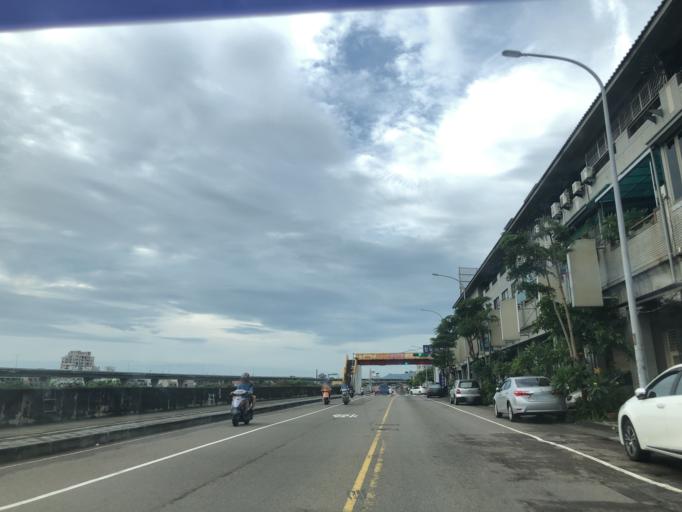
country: TW
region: Taiwan
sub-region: Taichung City
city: Taichung
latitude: 24.1033
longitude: 120.6954
